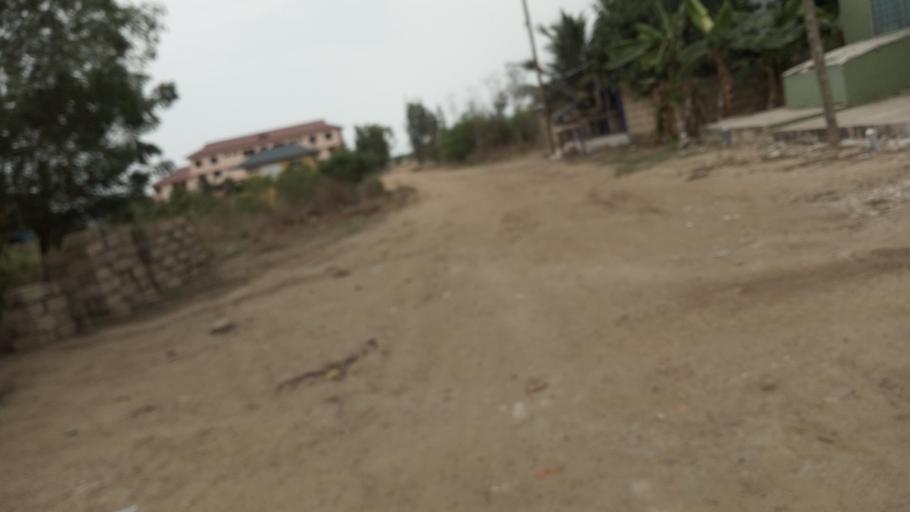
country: GH
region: Central
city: Winneba
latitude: 5.3802
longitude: -0.6388
